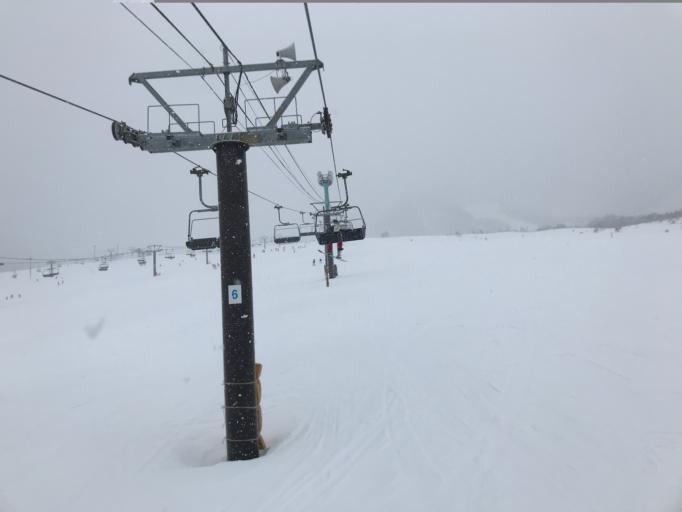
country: JP
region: Nagano
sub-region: Kitaazumi Gun
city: Hakuba
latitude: 36.7489
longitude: 137.8661
